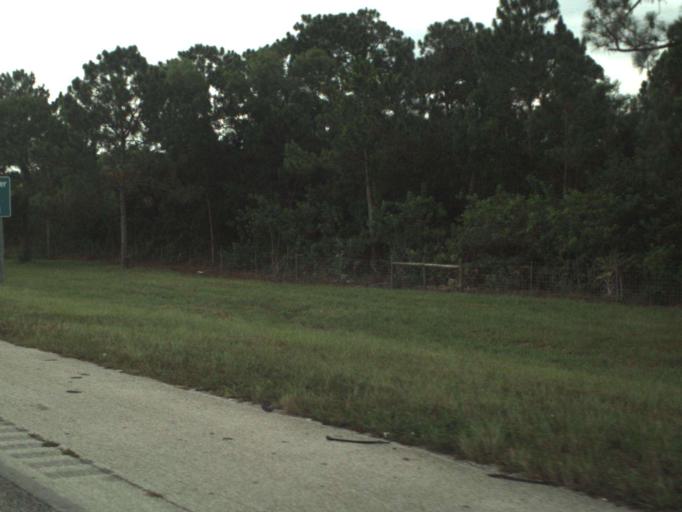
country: US
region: Florida
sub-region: Martin County
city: Palm City
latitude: 27.1267
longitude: -80.2883
